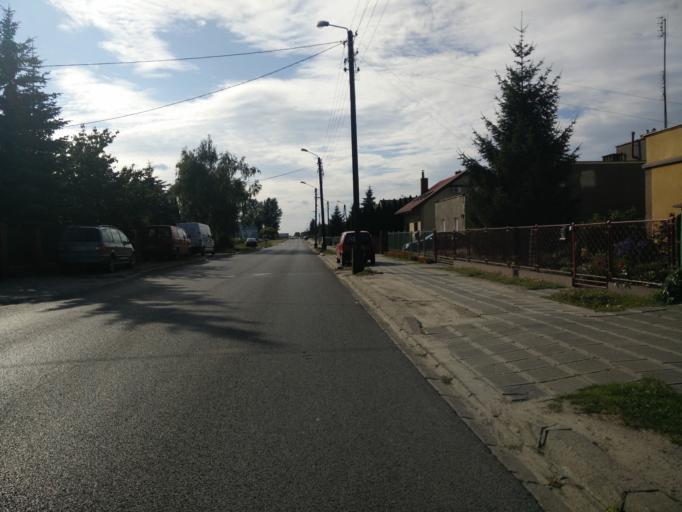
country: PL
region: Greater Poland Voivodeship
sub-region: Powiat sredzki
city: Sroda Wielkopolska
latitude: 52.2286
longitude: 17.2628
